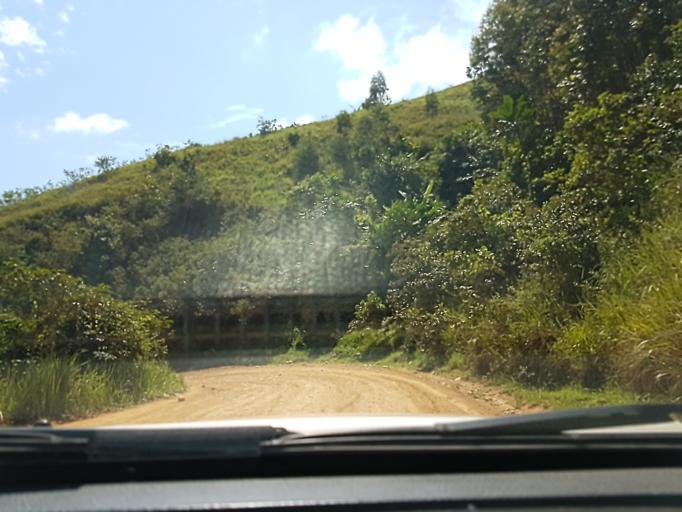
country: RW
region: Western Province
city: Cyangugu
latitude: -2.7030
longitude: 28.9106
